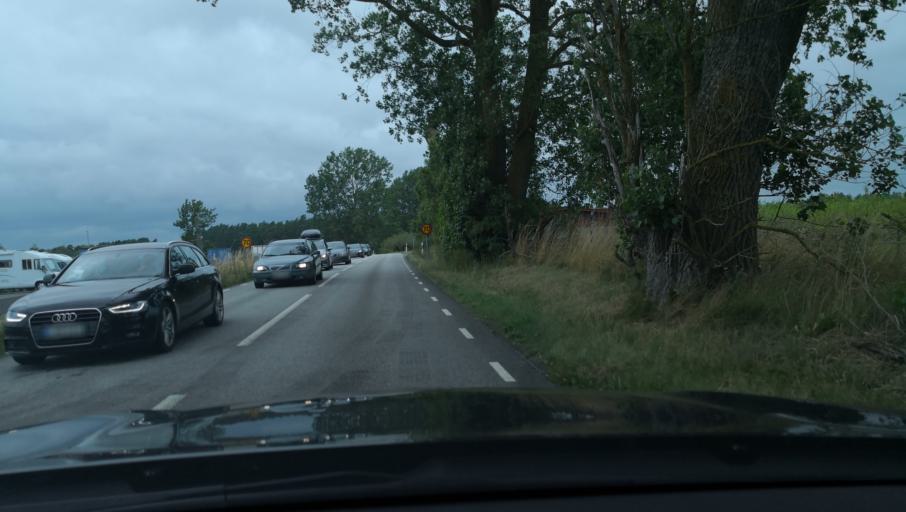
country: SE
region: Skane
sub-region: Simrishamns Kommun
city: Kivik
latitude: 55.7103
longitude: 14.1694
